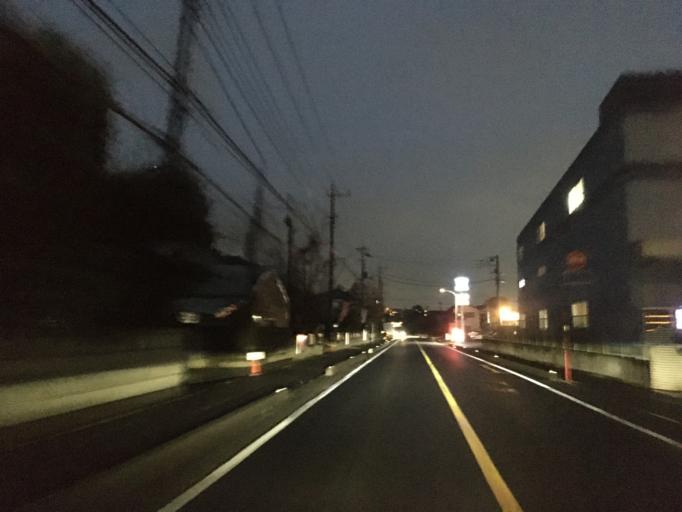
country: JP
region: Saitama
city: Oi
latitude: 35.8010
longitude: 139.5284
